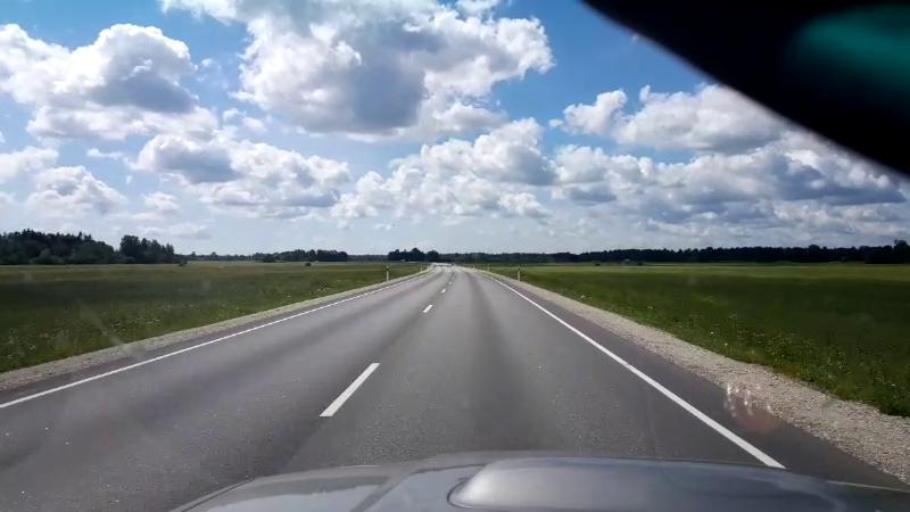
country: EE
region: Jaervamaa
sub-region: Jaerva-Jaani vald
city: Jarva-Jaani
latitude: 59.0914
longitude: 25.6901
